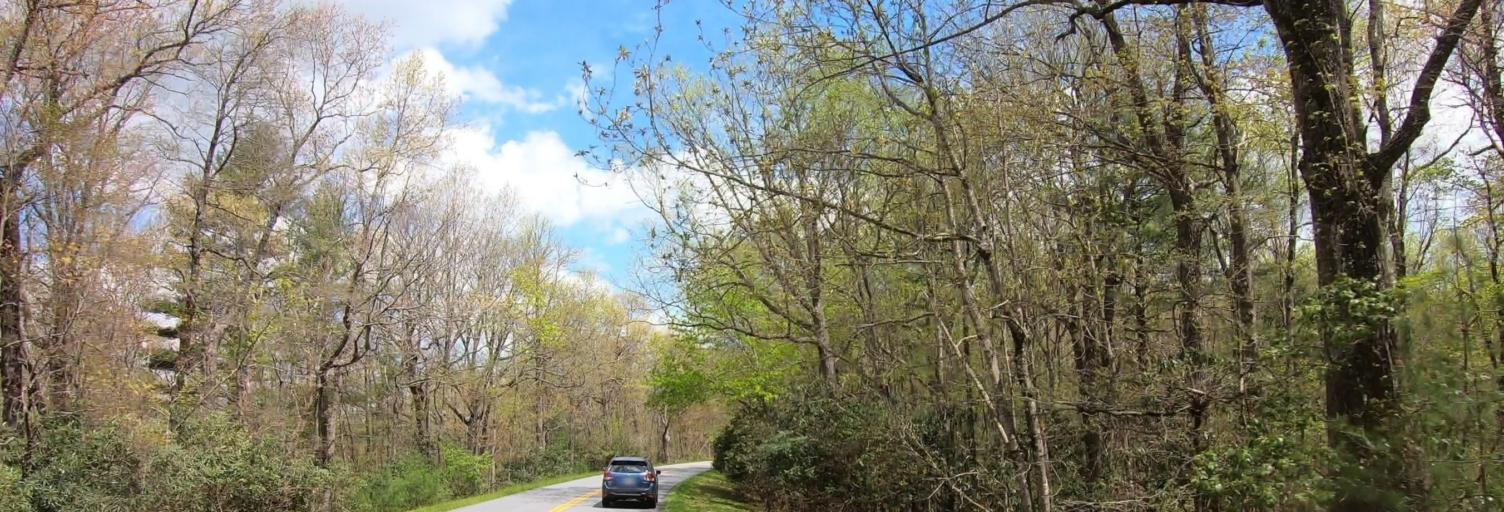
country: US
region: Virginia
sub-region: City of Galax
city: Galax
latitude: 36.5462
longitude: -80.9187
